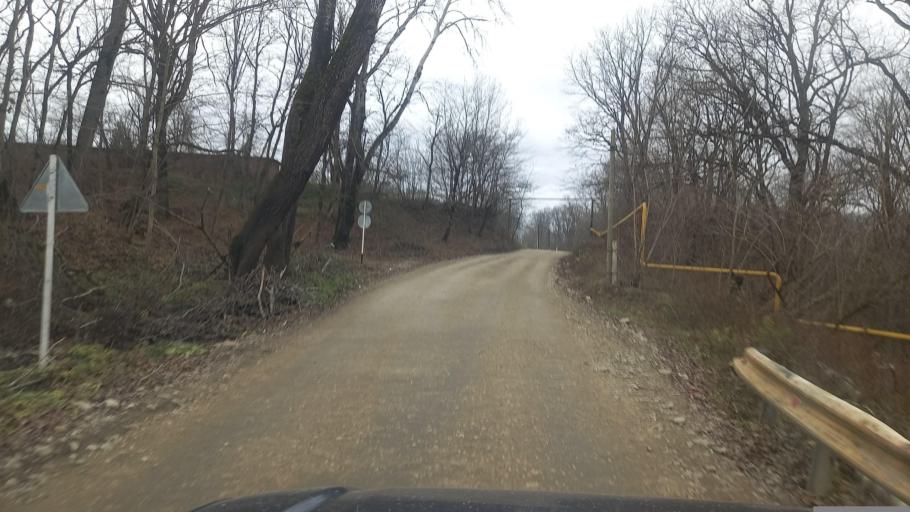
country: RU
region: Adygeya
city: Maykop
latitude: 44.5737
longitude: 40.0720
